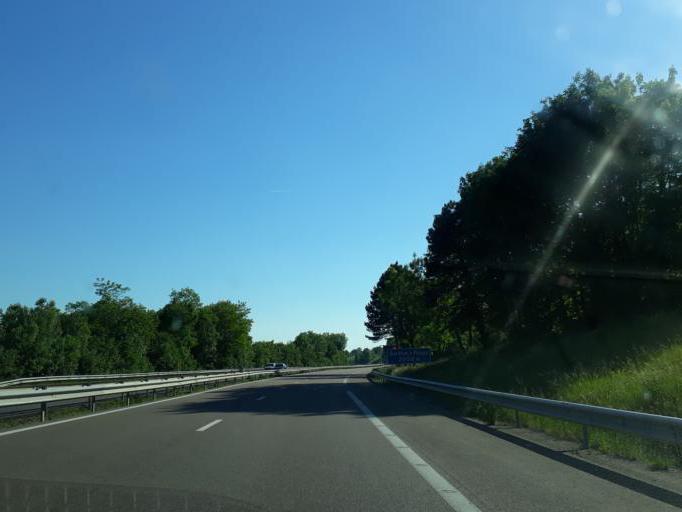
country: FR
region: Bourgogne
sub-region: Departement de la Cote-d'Or
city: Pouilly-en-Auxois
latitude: 47.2654
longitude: 4.5851
